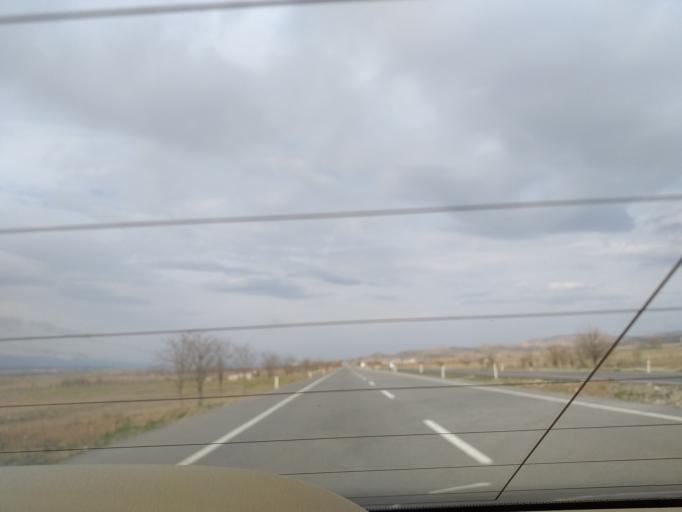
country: TR
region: Yozgat
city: Yerkoy
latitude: 39.6848
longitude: 34.4417
